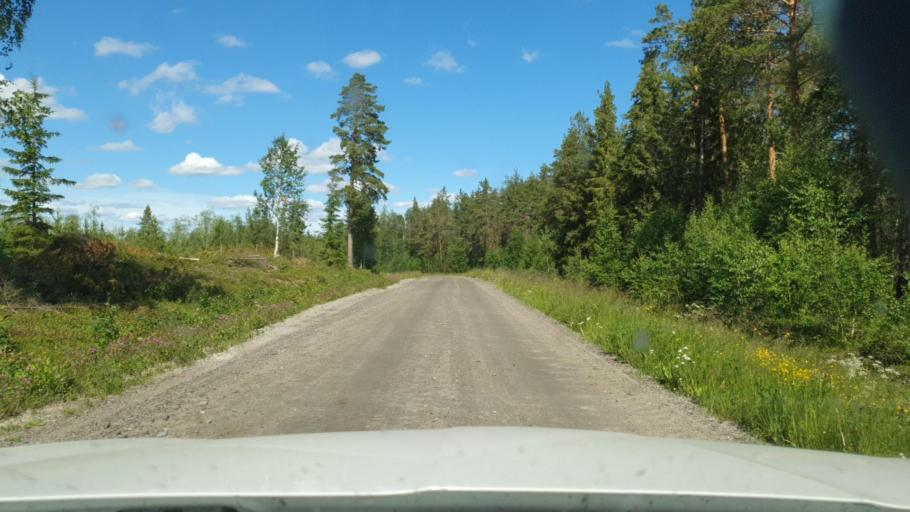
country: SE
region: Vaesterbotten
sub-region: Skelleftea Kommun
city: Byske
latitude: 65.1266
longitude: 21.2036
